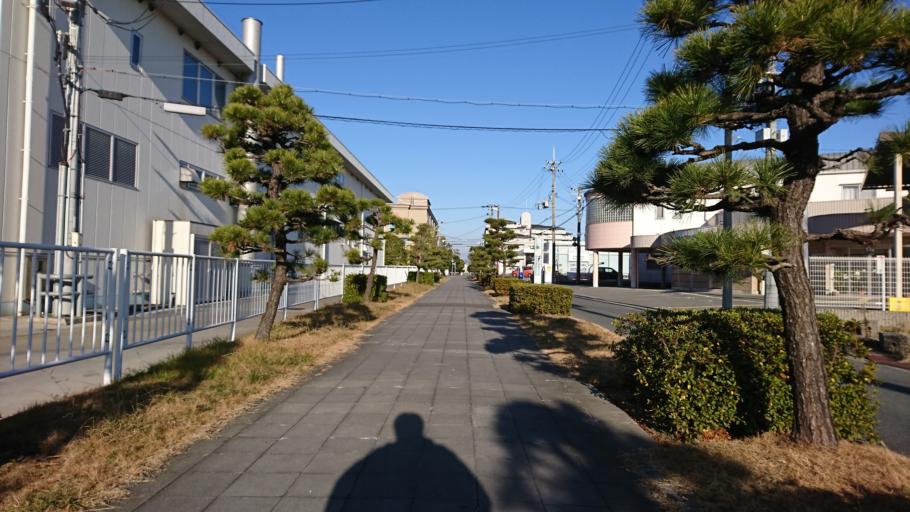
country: JP
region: Hyogo
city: Kakogawacho-honmachi
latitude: 34.7482
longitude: 134.8401
